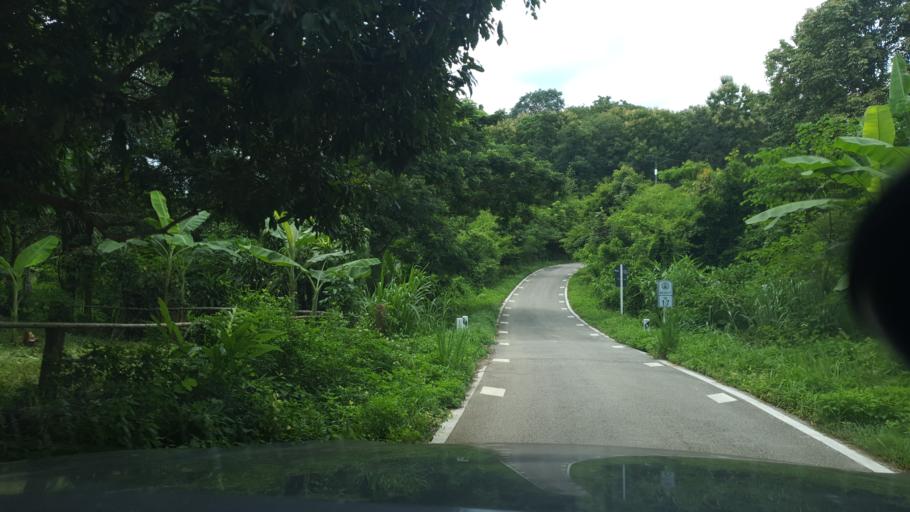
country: TH
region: Lampang
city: Hang Chat
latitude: 18.4176
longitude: 99.2642
